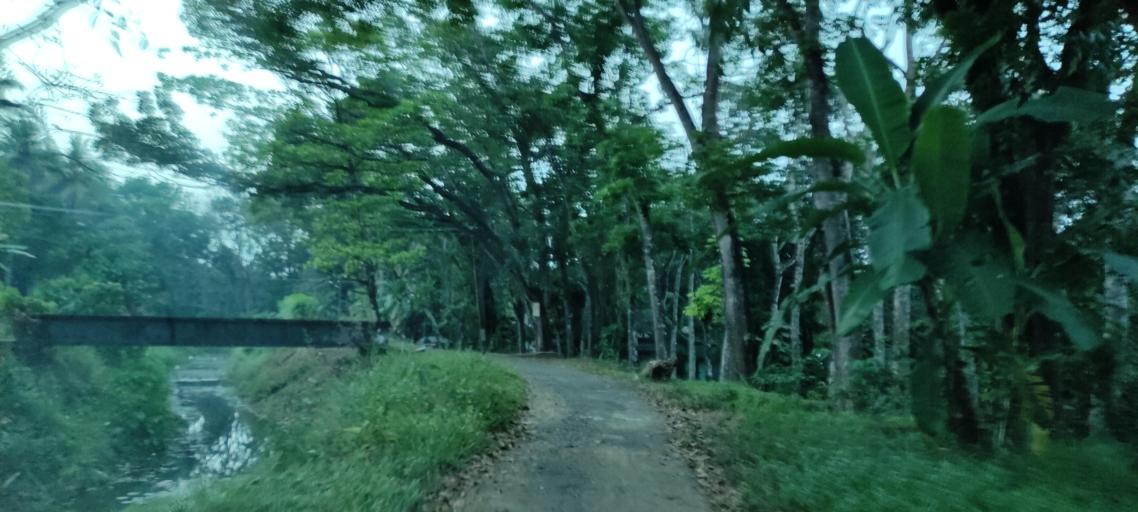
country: IN
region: Kerala
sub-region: Pattanamtitta
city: Adur
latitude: 9.1604
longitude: 76.7515
